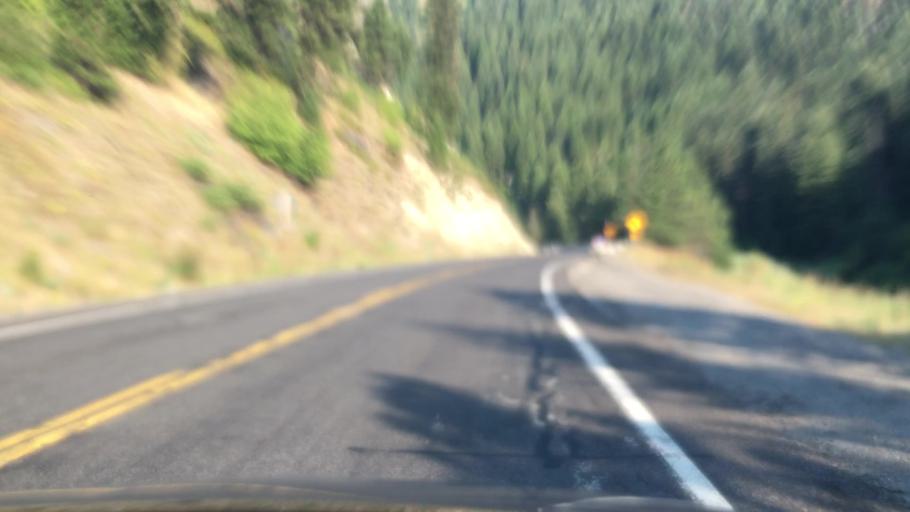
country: US
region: Idaho
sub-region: Valley County
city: Cascade
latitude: 44.2626
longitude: -116.0721
